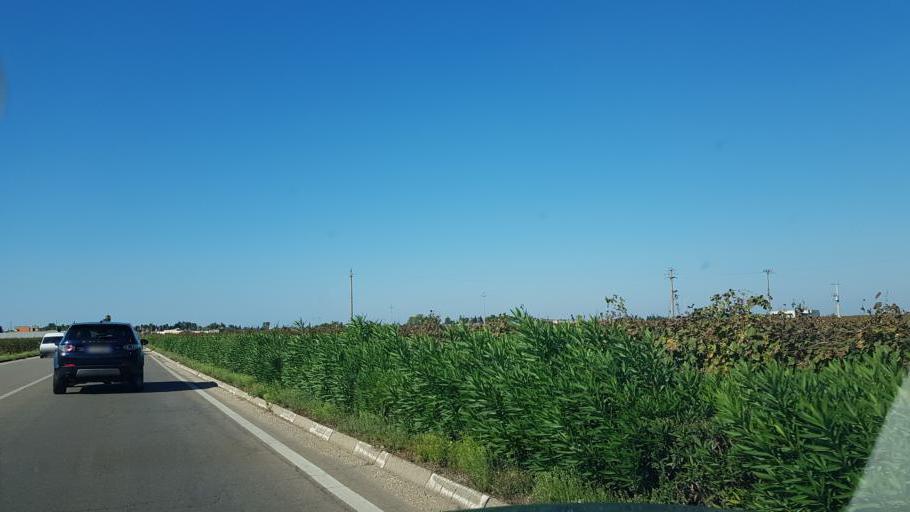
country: IT
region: Apulia
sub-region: Provincia di Lecce
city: Leverano
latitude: 40.2878
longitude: 17.9757
